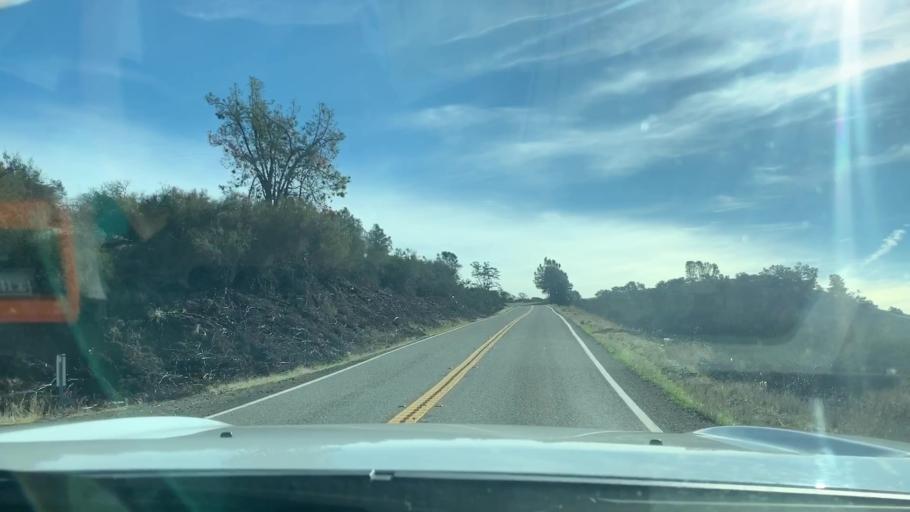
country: US
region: California
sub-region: Monterey County
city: King City
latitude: 36.2002
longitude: -120.7931
